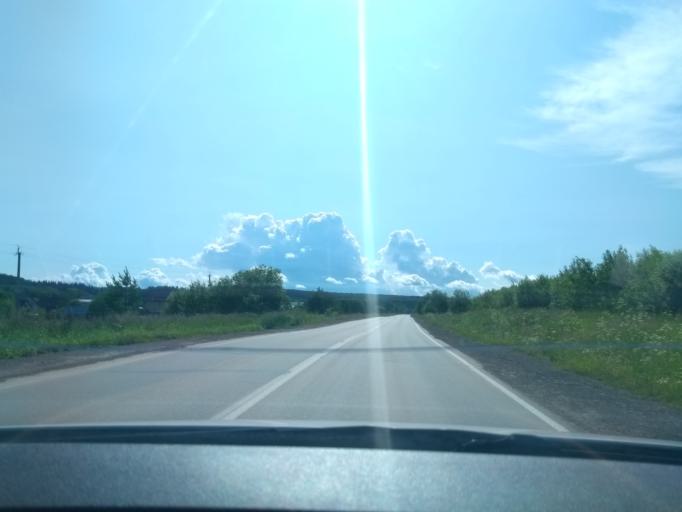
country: RU
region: Perm
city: Lobanovo
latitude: 57.8455
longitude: 56.3590
